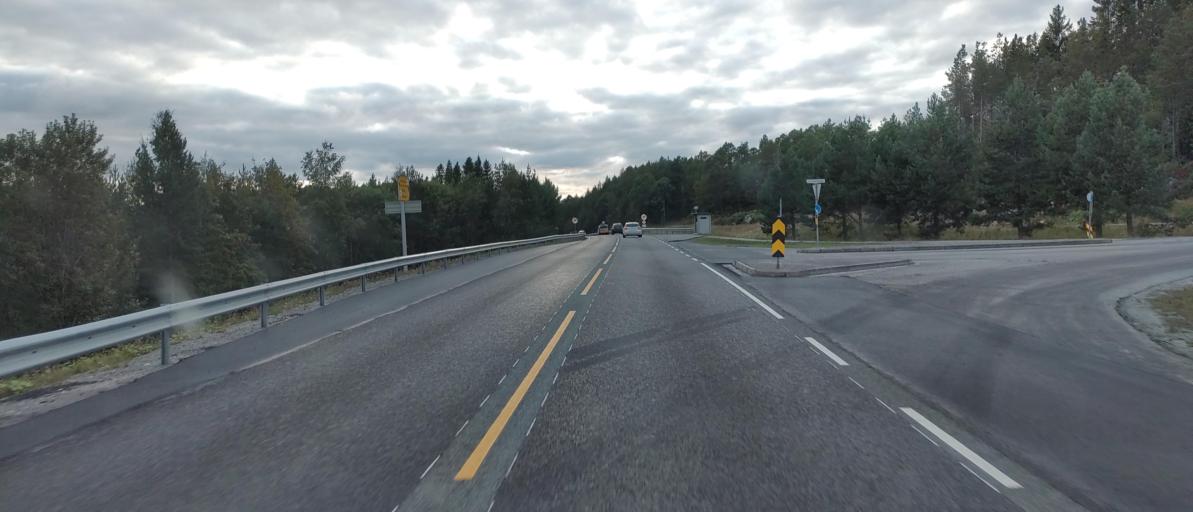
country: NO
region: More og Romsdal
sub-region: Molde
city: Hjelset
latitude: 62.7344
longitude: 7.3954
